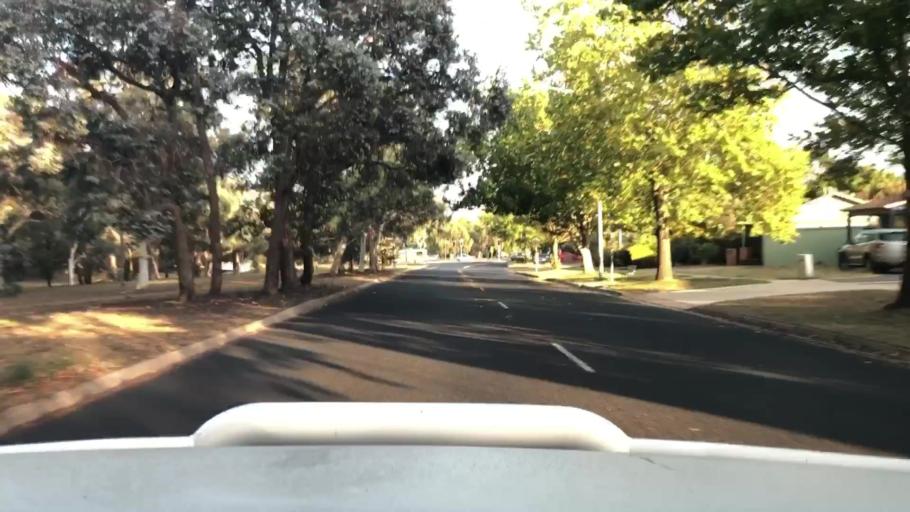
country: AU
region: Australian Capital Territory
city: Canberra
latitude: -35.2514
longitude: 149.1569
